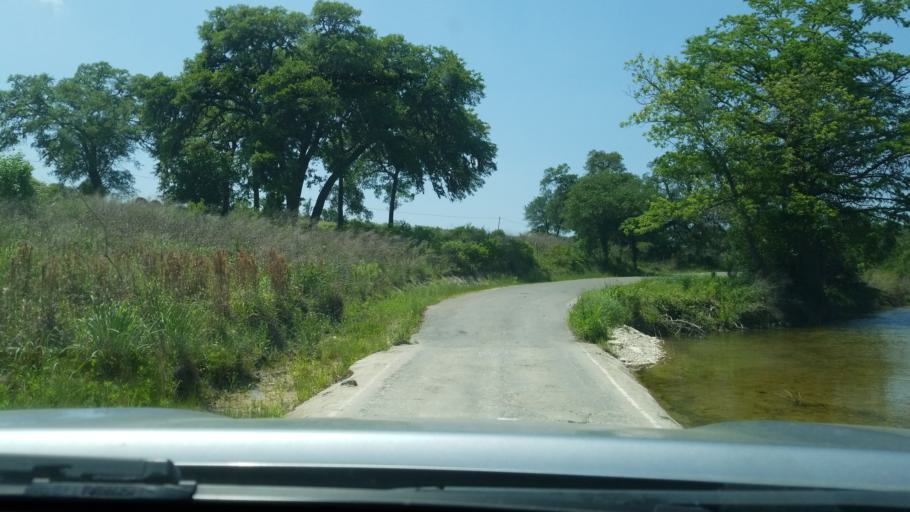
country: US
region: Texas
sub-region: Blanco County
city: Blanco
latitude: 30.0006
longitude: -98.4225
